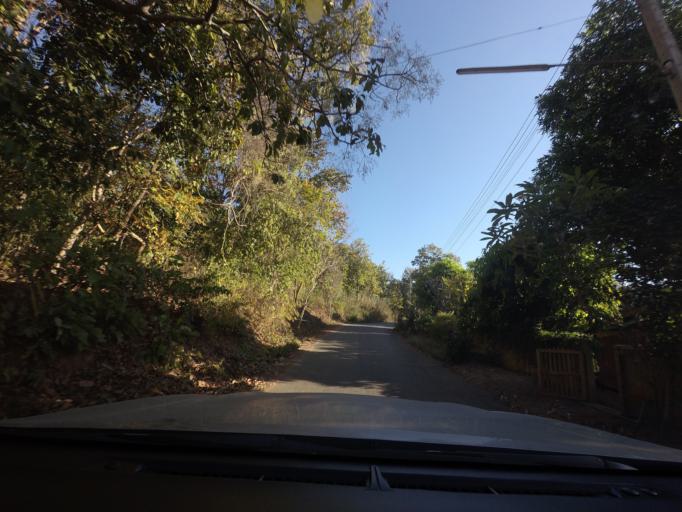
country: TH
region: Mae Hong Son
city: Mae Hi
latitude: 19.3502
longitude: 98.4524
